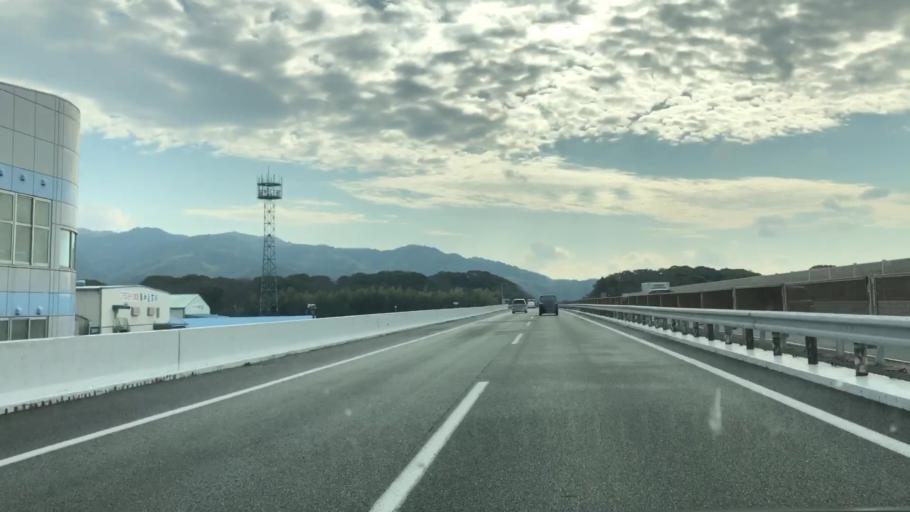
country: JP
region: Fukuoka
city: Setakamachi-takayanagi
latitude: 33.1855
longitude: 130.5189
